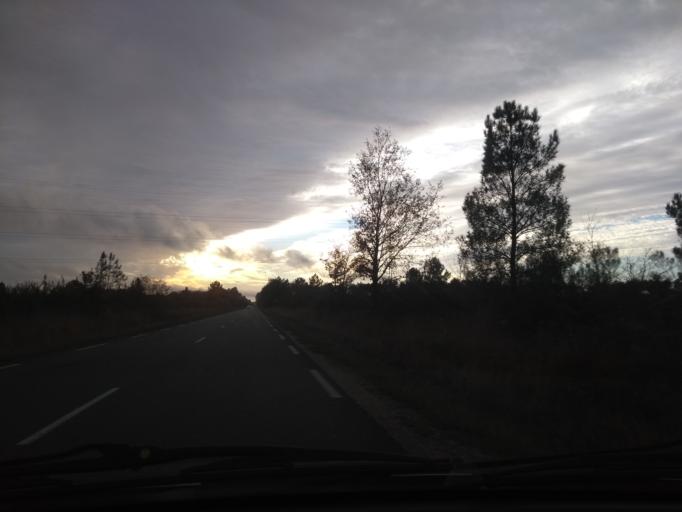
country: FR
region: Aquitaine
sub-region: Departement de la Gironde
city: Le Barp
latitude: 44.6113
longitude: -0.6871
